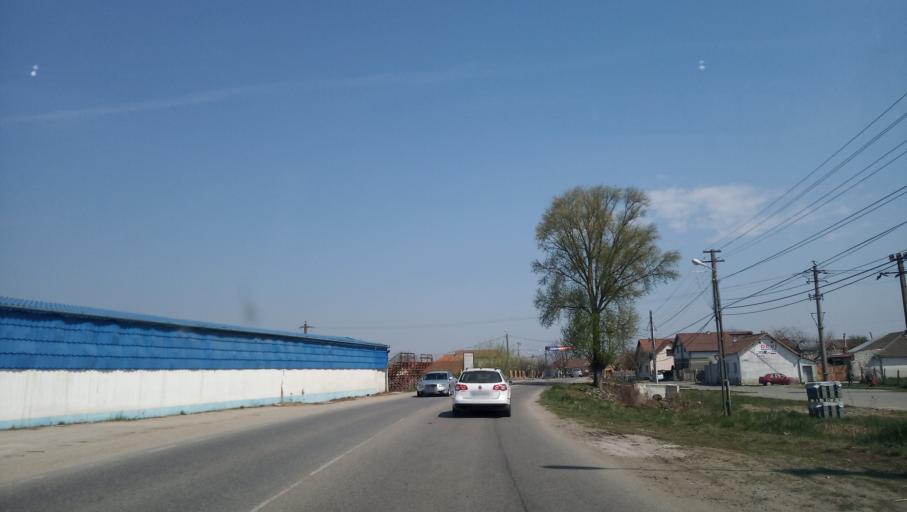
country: RO
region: Alba
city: Vurpar
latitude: 45.9965
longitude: 23.4880
